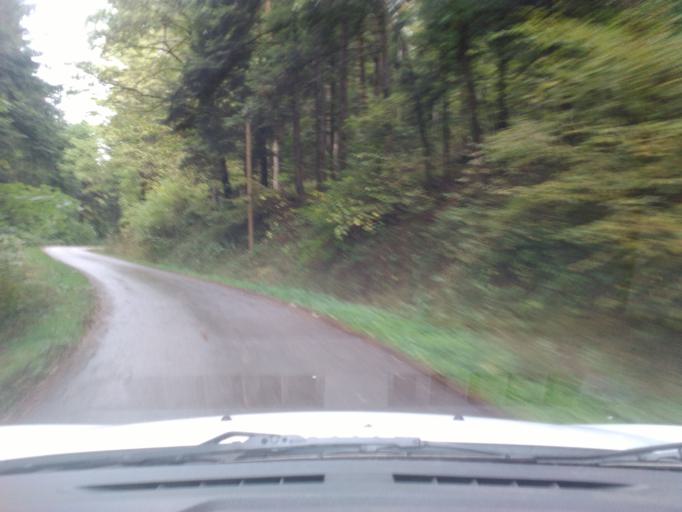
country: FR
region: Lorraine
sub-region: Departement des Vosges
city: Saint-Die-des-Vosges
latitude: 48.3074
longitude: 6.9767
